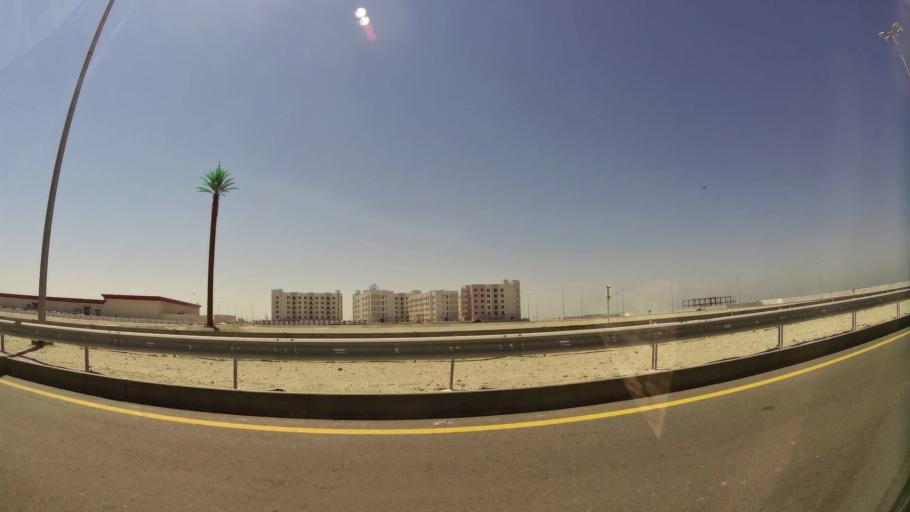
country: BH
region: Muharraq
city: Al Muharraq
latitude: 26.3099
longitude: 50.6238
